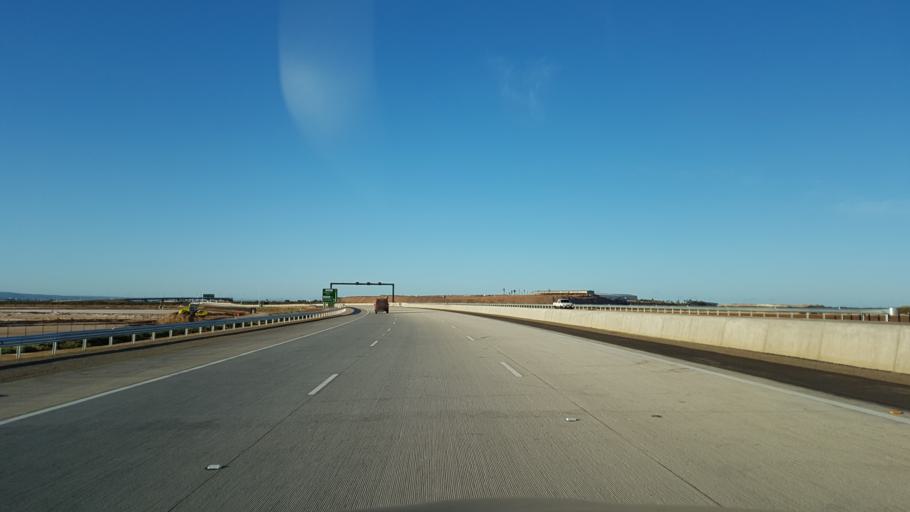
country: AU
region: South Australia
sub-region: Port Adelaide Enfield
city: Enfield
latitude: -34.8146
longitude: 138.5624
